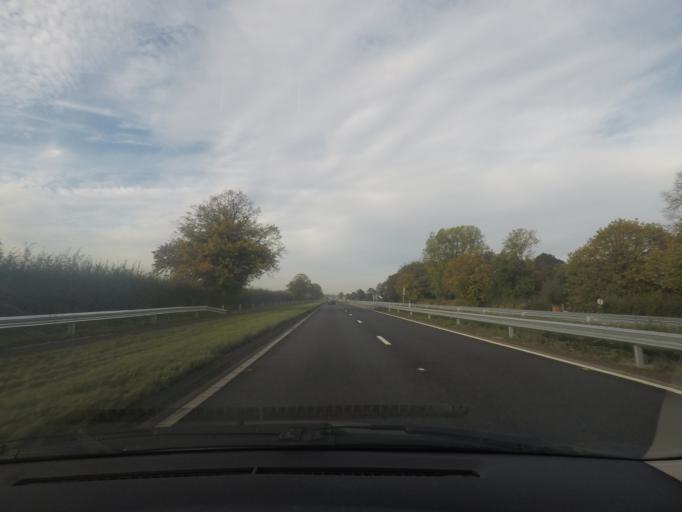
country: GB
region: England
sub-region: City of York
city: Copmanthorpe
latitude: 53.9188
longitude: -1.1599
